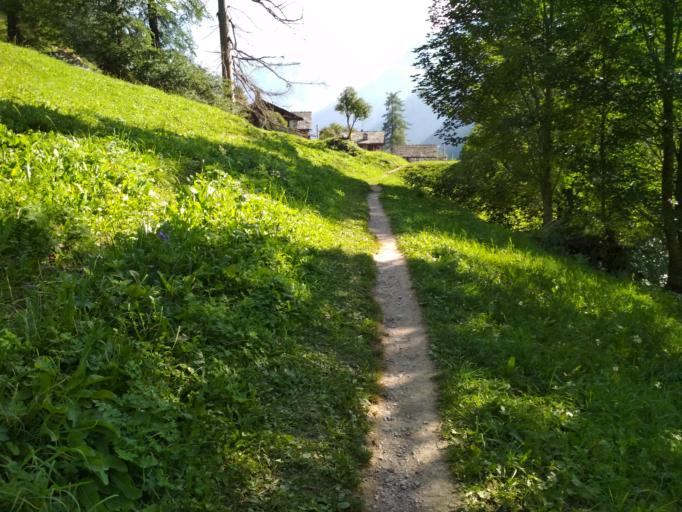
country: IT
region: Aosta Valley
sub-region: Valle d'Aosta
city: Gressoney-Saint-Jean
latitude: 45.8005
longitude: 7.8264
